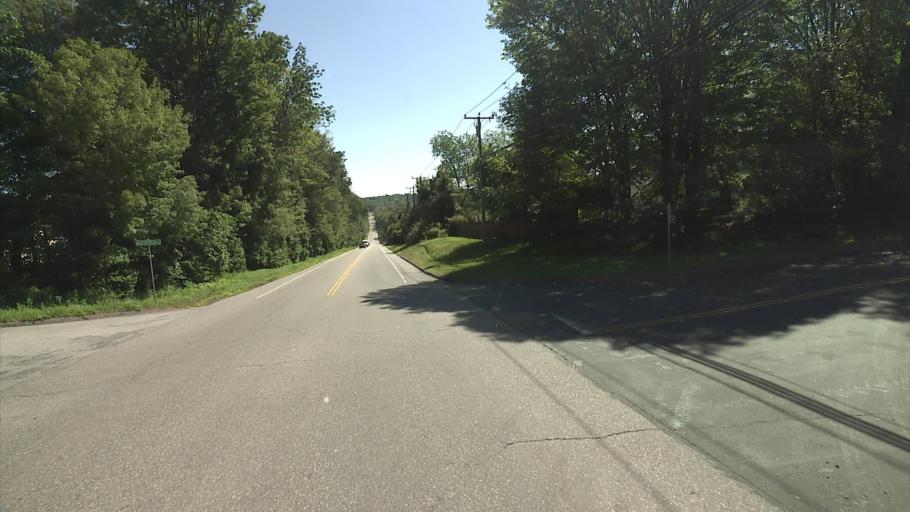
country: US
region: Connecticut
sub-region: New London County
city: Colchester
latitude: 41.5647
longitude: -72.3520
